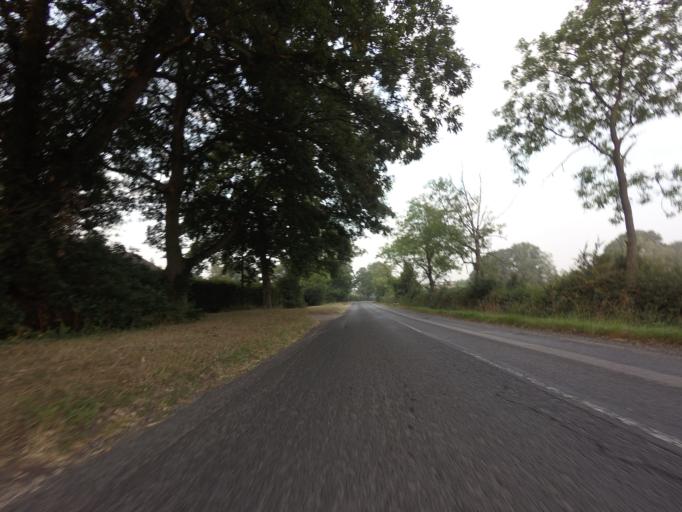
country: GB
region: England
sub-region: Kent
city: Lenham
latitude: 51.1660
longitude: 0.7365
